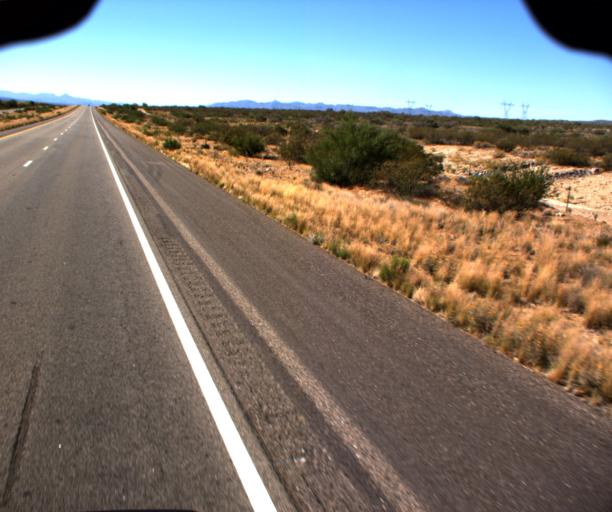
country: US
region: Arizona
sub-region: Mohave County
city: Kingman
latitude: 34.8857
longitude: -113.6501
